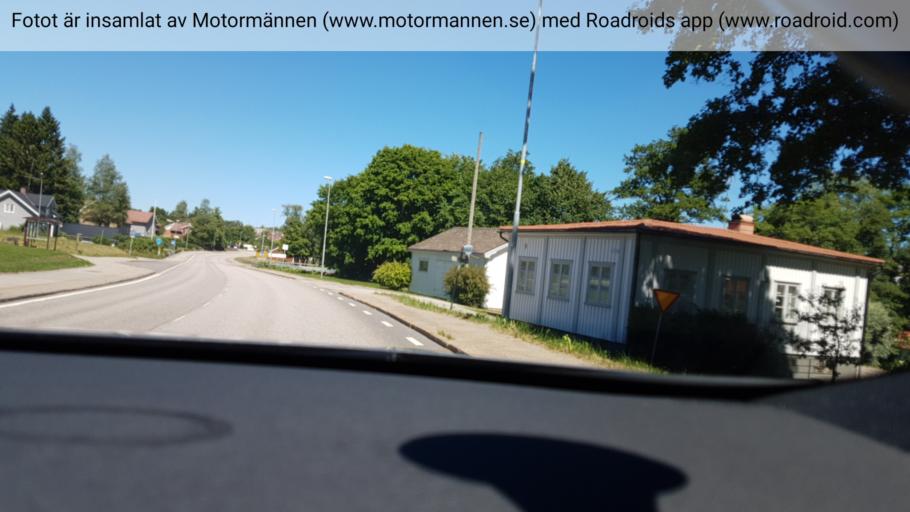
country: SE
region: Vaestra Goetaland
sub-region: Ulricehamns Kommun
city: Ulricehamn
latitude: 57.9269
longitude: 13.4942
